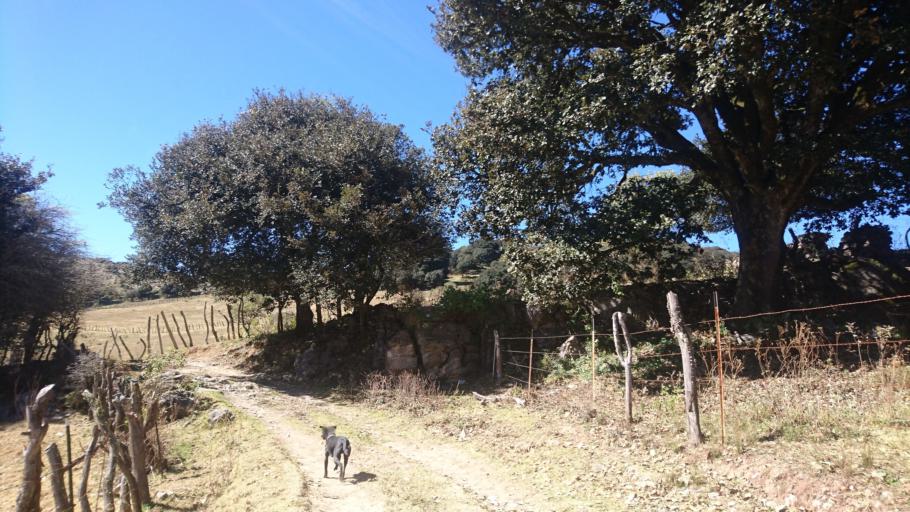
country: MX
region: San Luis Potosi
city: Zaragoza
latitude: 22.0218
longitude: -100.6199
